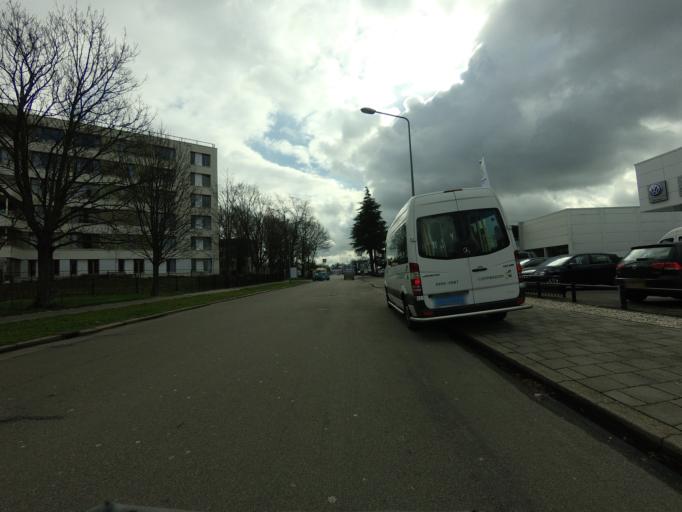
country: NL
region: North Holland
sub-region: Gemeente Wijdemeren
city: Nieuw-Loosdrecht
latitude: 52.2148
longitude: 5.1449
